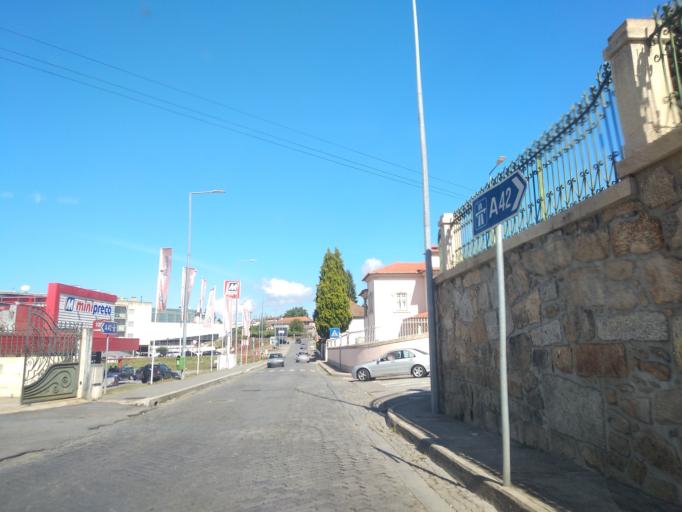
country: PT
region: Porto
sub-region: Pacos de Ferreira
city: Freamunde
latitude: 41.2870
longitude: -8.3353
